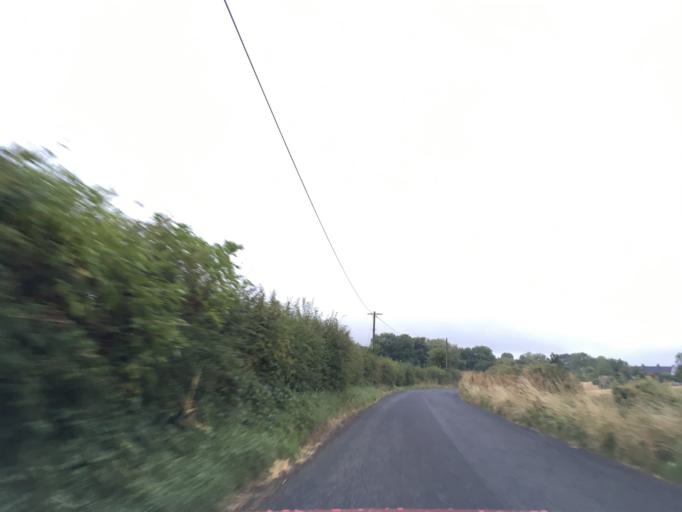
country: IE
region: Munster
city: Cahir
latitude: 52.4598
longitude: -7.9713
